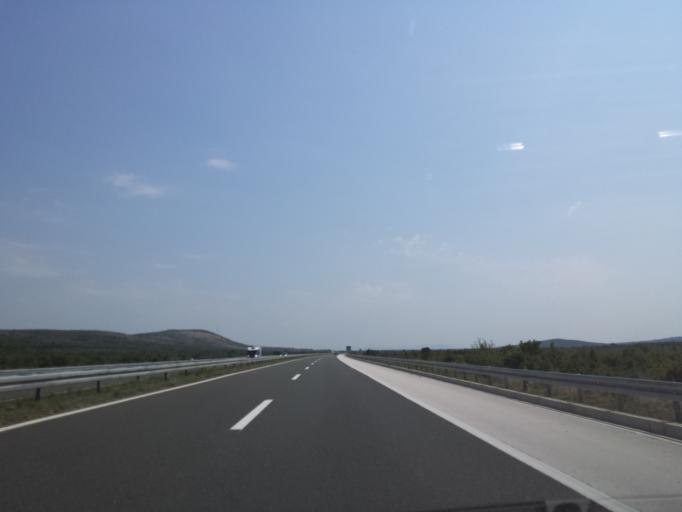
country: HR
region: Zadarska
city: Benkovac
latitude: 43.9534
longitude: 15.6804
